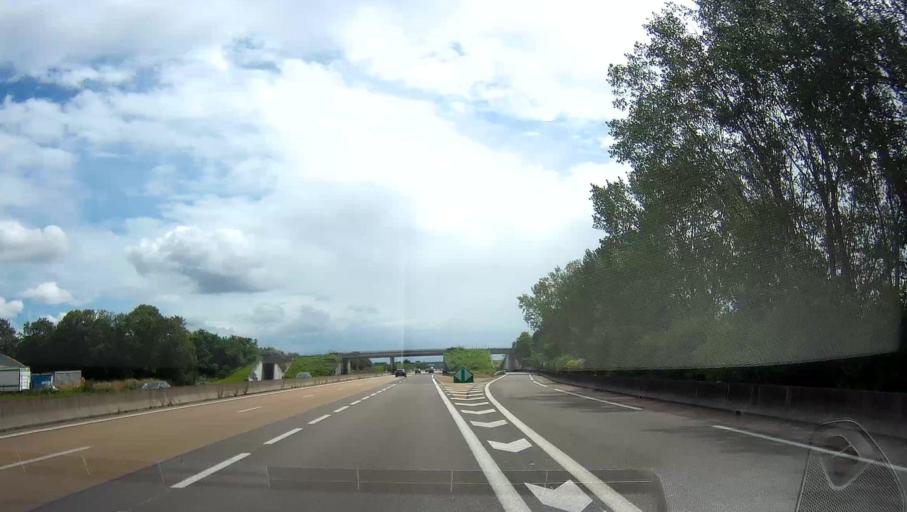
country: FR
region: Bourgogne
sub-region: Departement de la Cote-d'Or
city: Couternon
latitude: 47.3492
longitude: 5.1631
